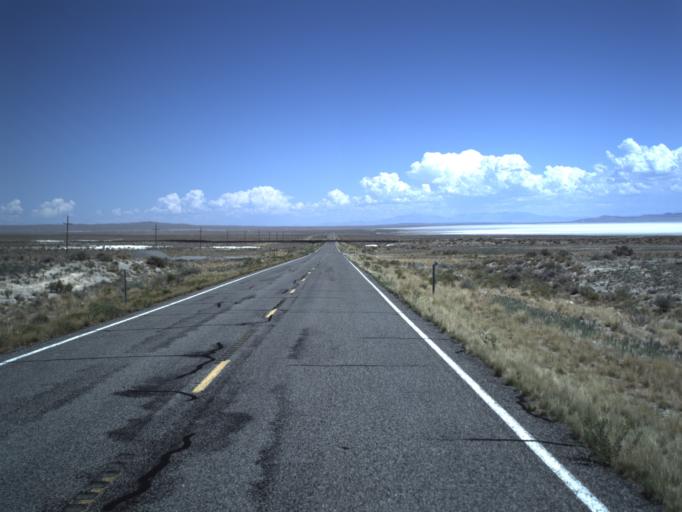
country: US
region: Utah
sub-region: Beaver County
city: Milford
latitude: 39.0581
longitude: -113.2517
